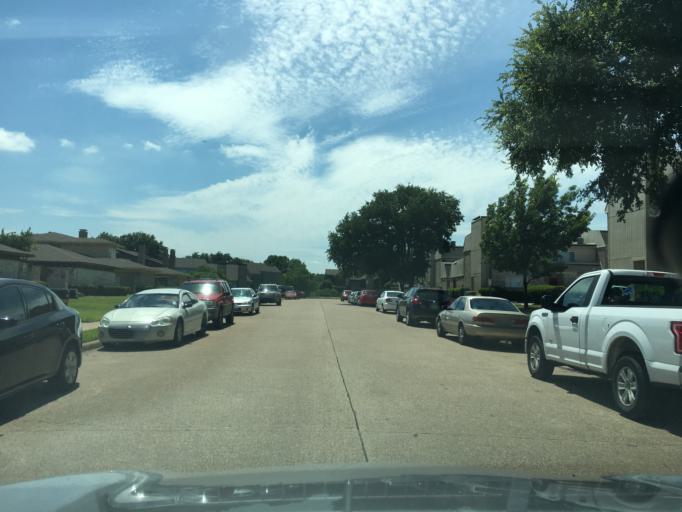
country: US
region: Texas
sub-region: Dallas County
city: Richardson
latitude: 32.9430
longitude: -96.6847
